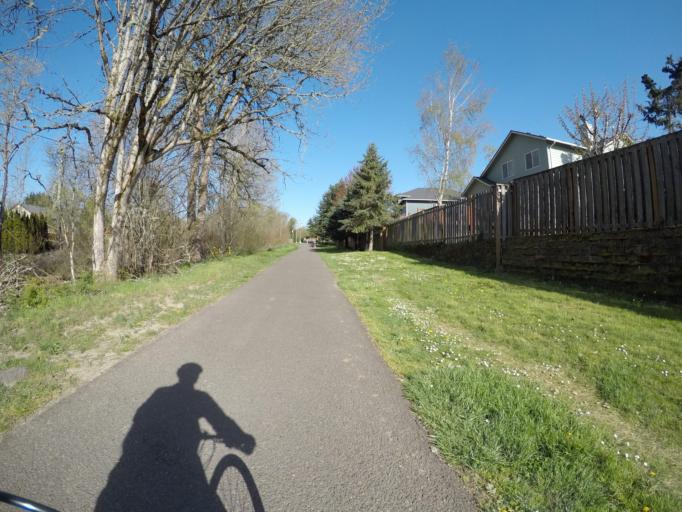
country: US
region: Oregon
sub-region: Washington County
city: Oak Hills
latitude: 45.5612
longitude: -122.8357
